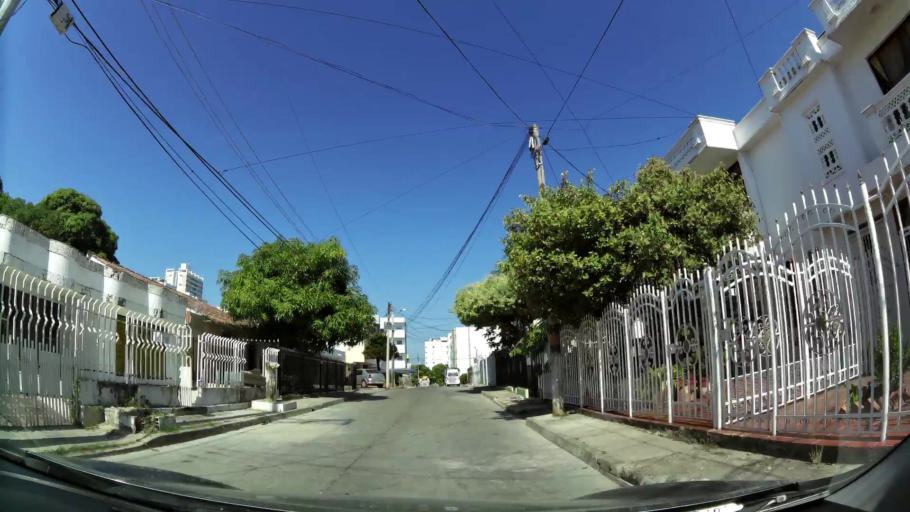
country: CO
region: Bolivar
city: Cartagena
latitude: 10.3890
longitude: -75.4723
